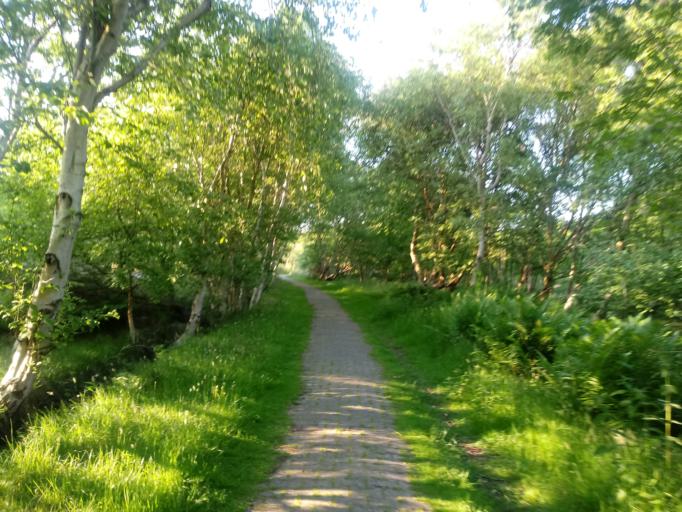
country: DE
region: Lower Saxony
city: Baltrum
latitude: 53.7281
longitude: 7.3951
